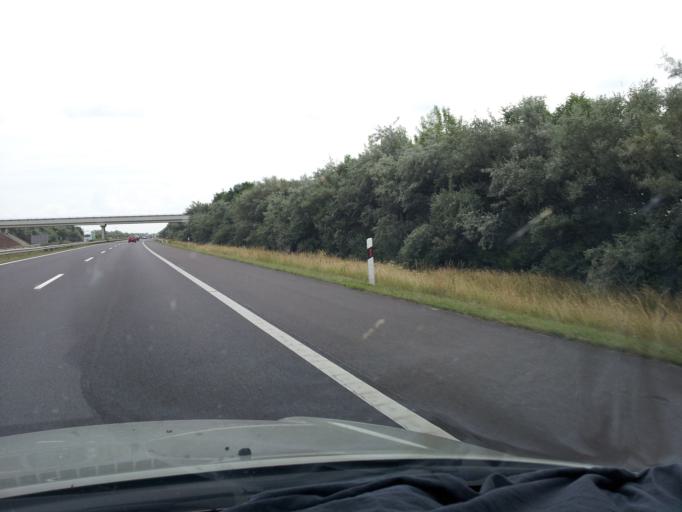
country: HU
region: Heves
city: Fuzesabony
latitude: 47.7290
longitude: 20.3614
